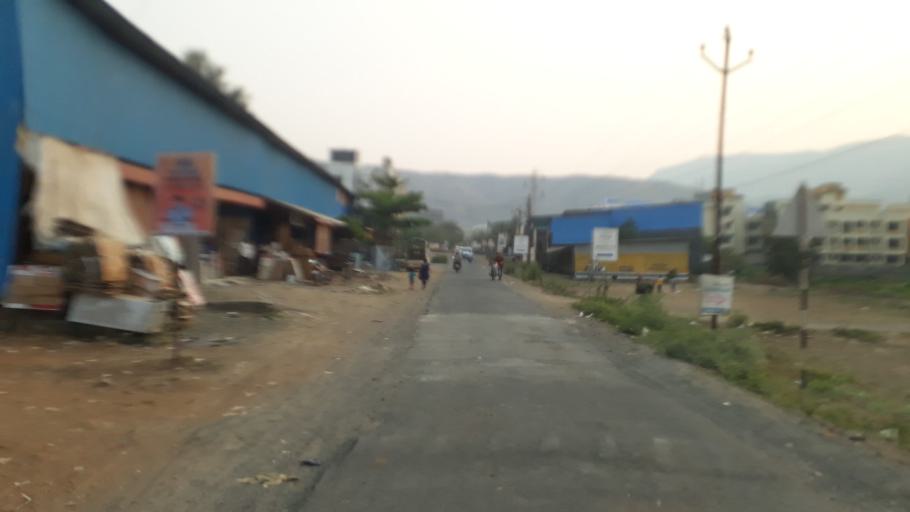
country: IN
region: Maharashtra
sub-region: Raigarh
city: Neral
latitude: 19.0268
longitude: 73.3225
